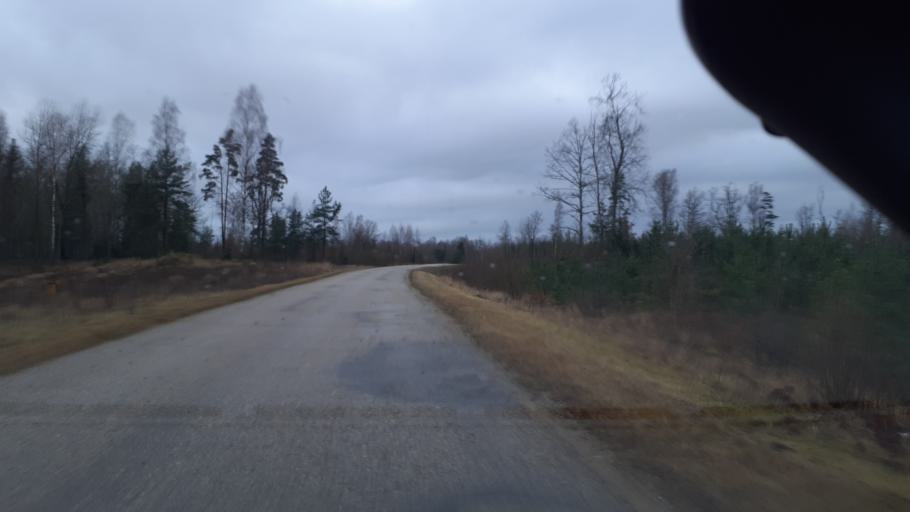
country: LV
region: Kuldigas Rajons
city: Kuldiga
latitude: 56.8739
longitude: 21.8514
